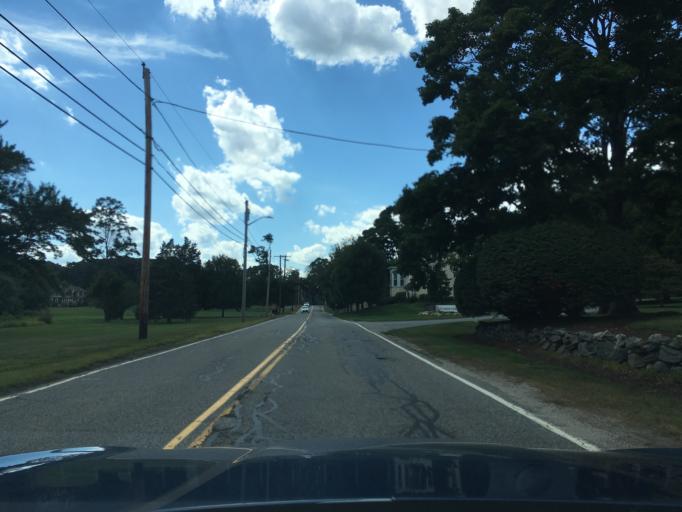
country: US
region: Rhode Island
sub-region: Bristol County
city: Barrington
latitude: 41.7487
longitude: -71.3235
